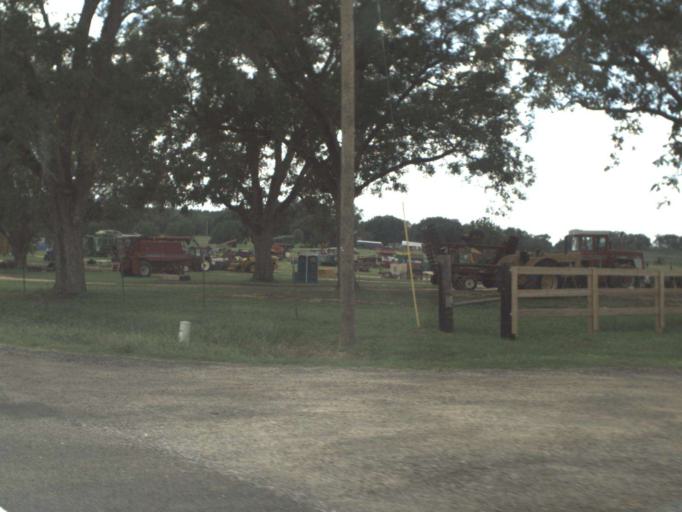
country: US
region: Florida
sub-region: Jackson County
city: Graceville
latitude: 30.9725
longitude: -85.4093
